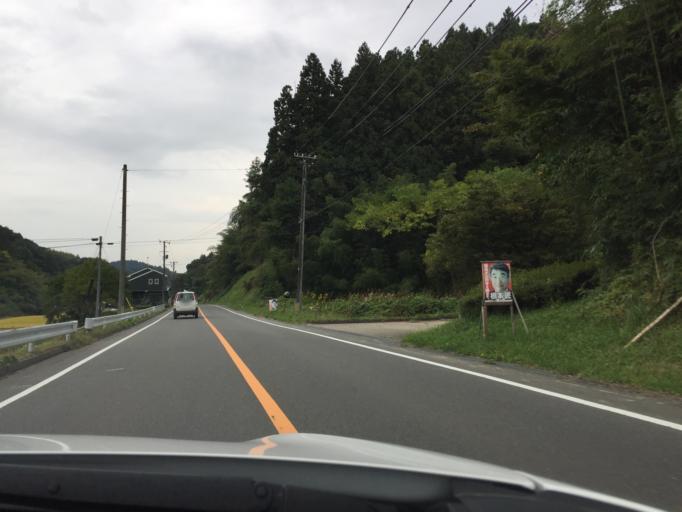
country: JP
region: Fukushima
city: Nihommatsu
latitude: 37.6018
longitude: 140.5359
